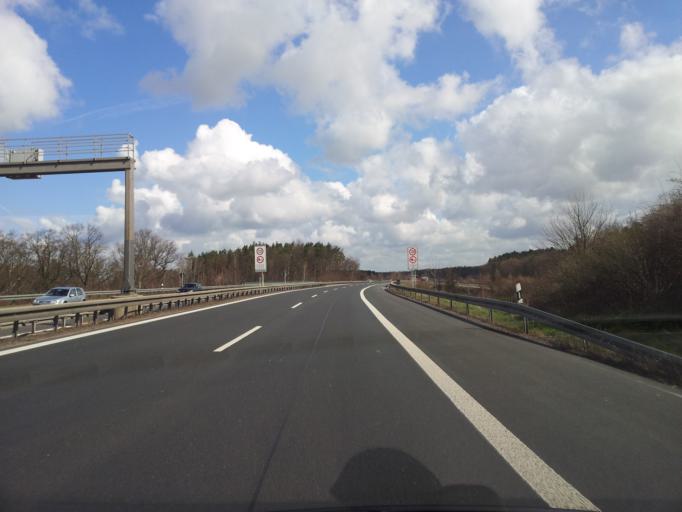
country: DE
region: Saxony
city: Albertstadt
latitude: 51.1348
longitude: 13.7511
